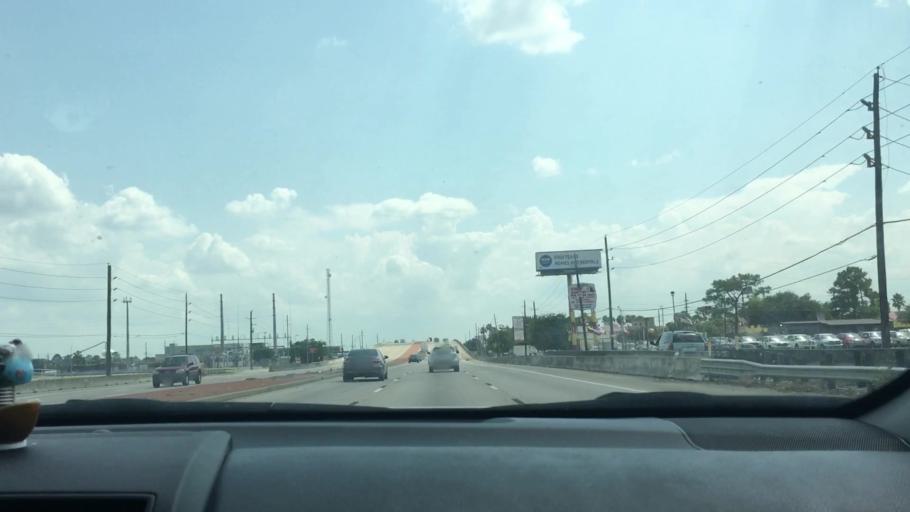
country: US
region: Texas
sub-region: Fort Bend County
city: Mission Bend
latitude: 29.7153
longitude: -95.6443
